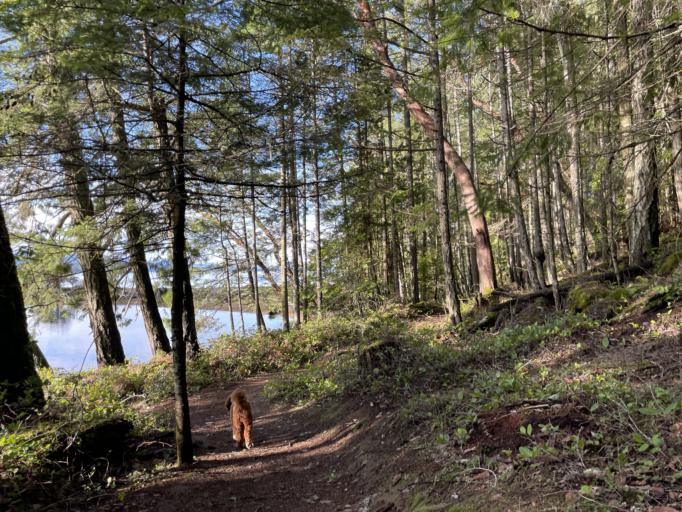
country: CA
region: British Columbia
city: North Saanich
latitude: 48.8981
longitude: -123.4063
